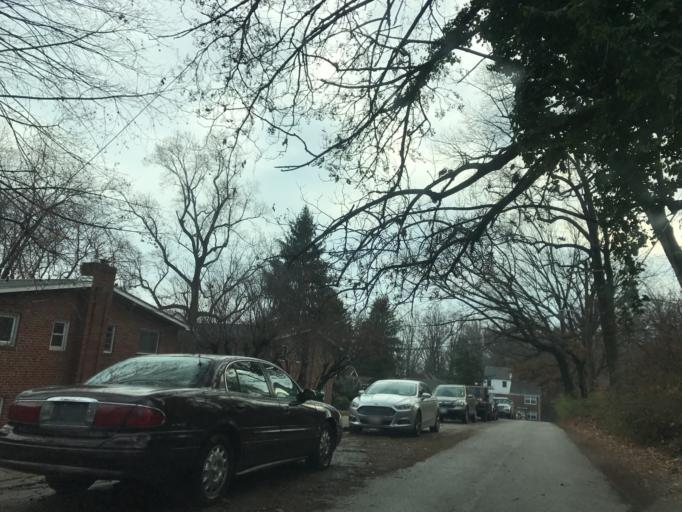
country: US
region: Maryland
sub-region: Baltimore County
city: Overlea
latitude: 39.3555
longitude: -76.5381
